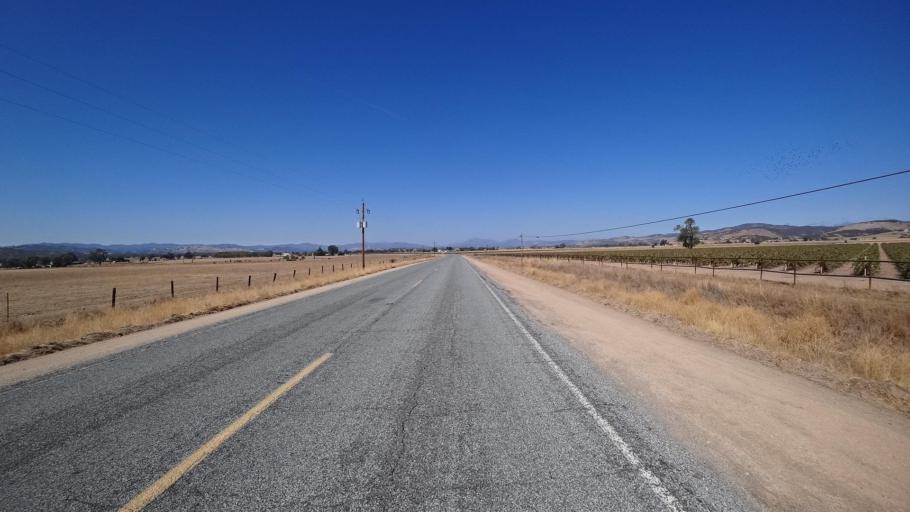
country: US
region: California
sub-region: San Luis Obispo County
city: Lake Nacimiento
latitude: 35.9343
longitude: -121.0603
